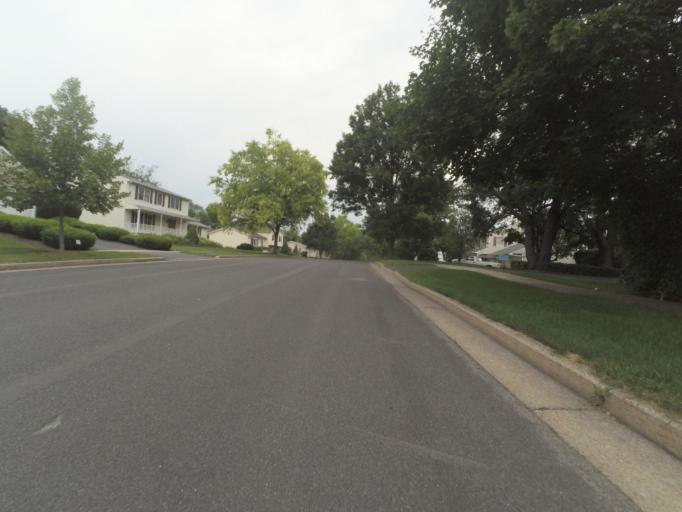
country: US
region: Pennsylvania
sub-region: Centre County
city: State College
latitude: 40.7740
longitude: -77.8676
